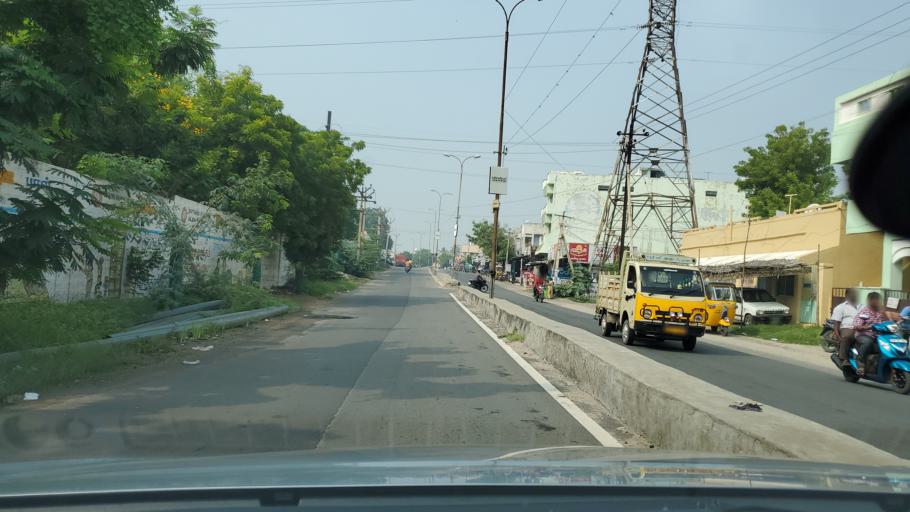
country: IN
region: Tamil Nadu
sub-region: Erode
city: Erode
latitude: 11.3263
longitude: 77.7190
